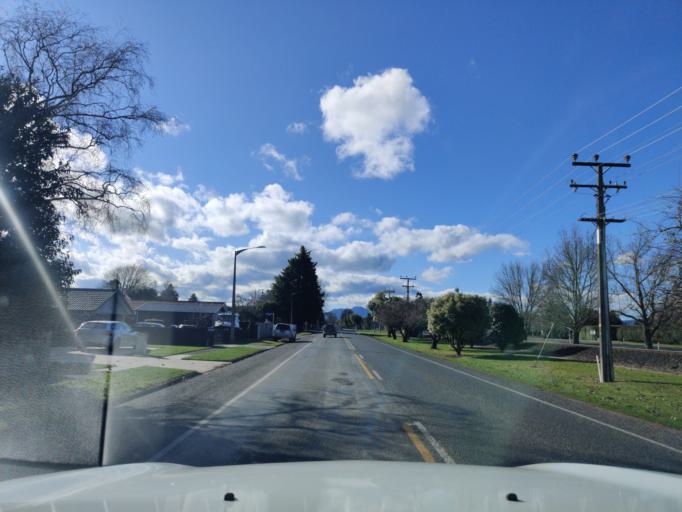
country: NZ
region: Waikato
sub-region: Matamata-Piako District
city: Matamata
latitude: -37.8269
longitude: 175.7692
